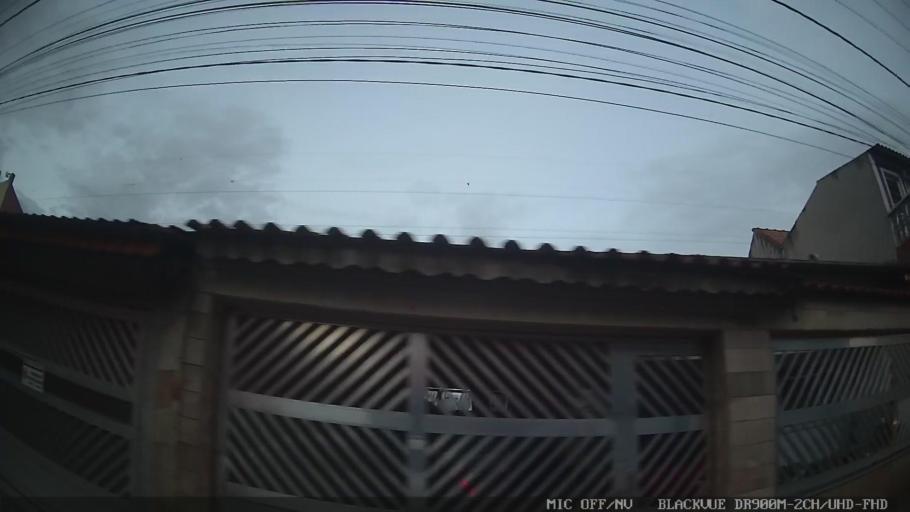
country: BR
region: Sao Paulo
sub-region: Itaquaquecetuba
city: Itaquaquecetuba
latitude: -23.4661
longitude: -46.3435
